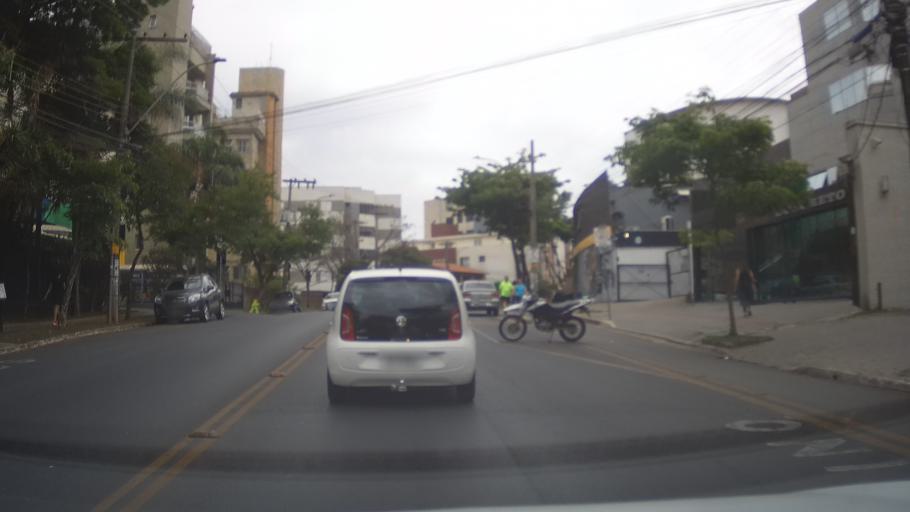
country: BR
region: Minas Gerais
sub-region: Belo Horizonte
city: Belo Horizonte
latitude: -19.9512
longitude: -43.9223
